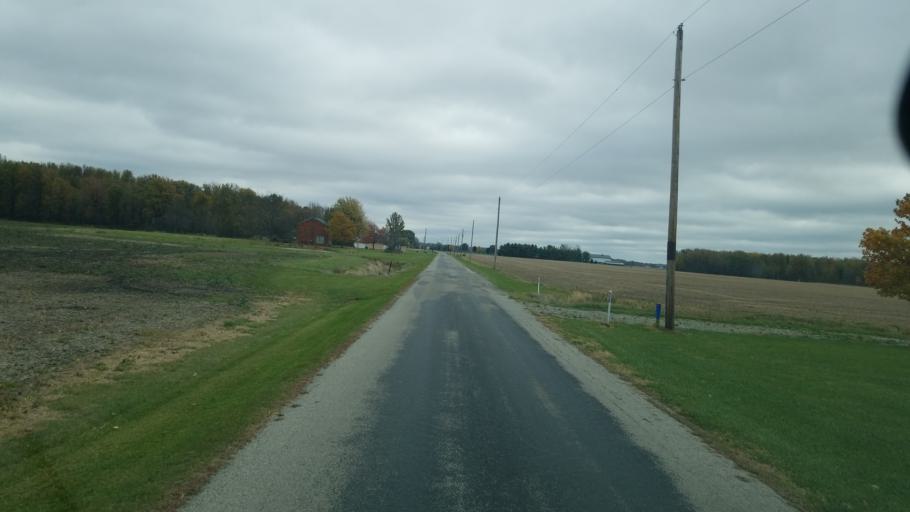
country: US
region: Ohio
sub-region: Huron County
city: Willard
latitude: 40.9316
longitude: -82.8415
